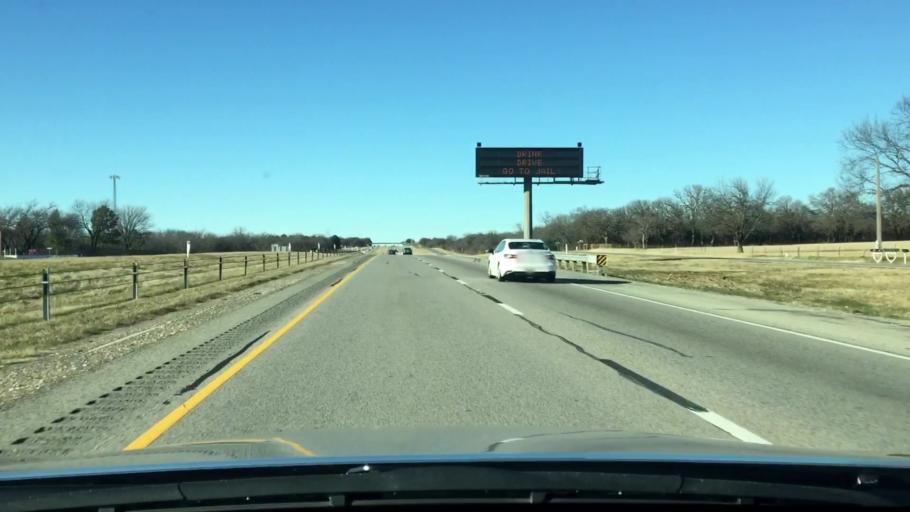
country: US
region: Texas
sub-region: Johnson County
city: Alvarado
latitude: 32.3676
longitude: -97.2013
